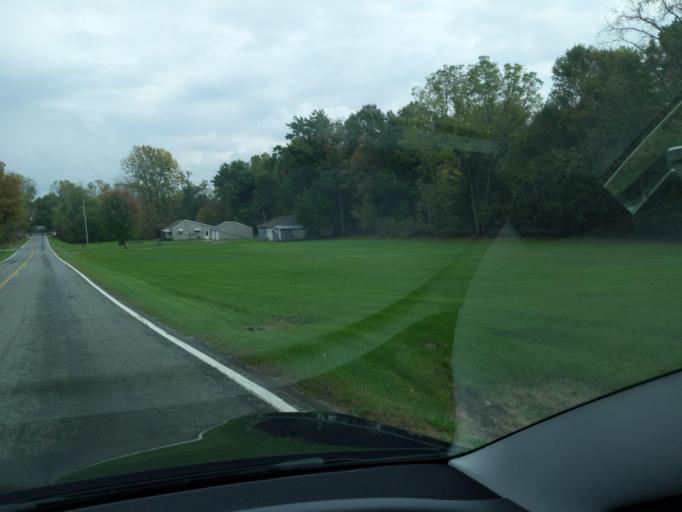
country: US
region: Michigan
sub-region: Eaton County
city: Eaton Rapids
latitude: 42.4657
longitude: -84.5715
